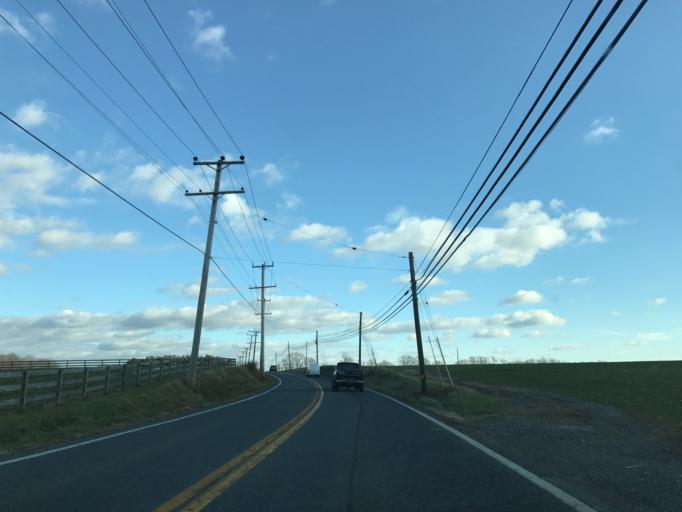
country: US
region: Maryland
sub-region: Harford County
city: Jarrettsville
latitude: 39.6146
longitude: -76.5397
